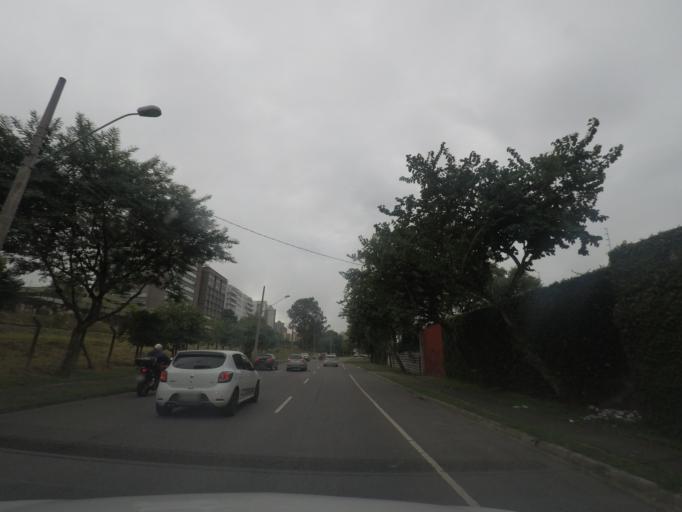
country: BR
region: Parana
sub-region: Curitiba
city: Curitiba
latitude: -25.4363
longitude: -49.2482
